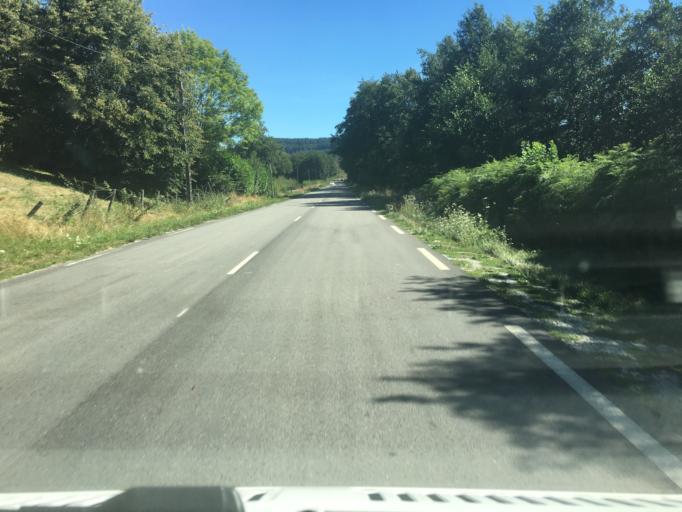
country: FR
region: Limousin
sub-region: Departement de la Correze
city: Bort-les-Orgues
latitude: 45.4296
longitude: 2.4554
